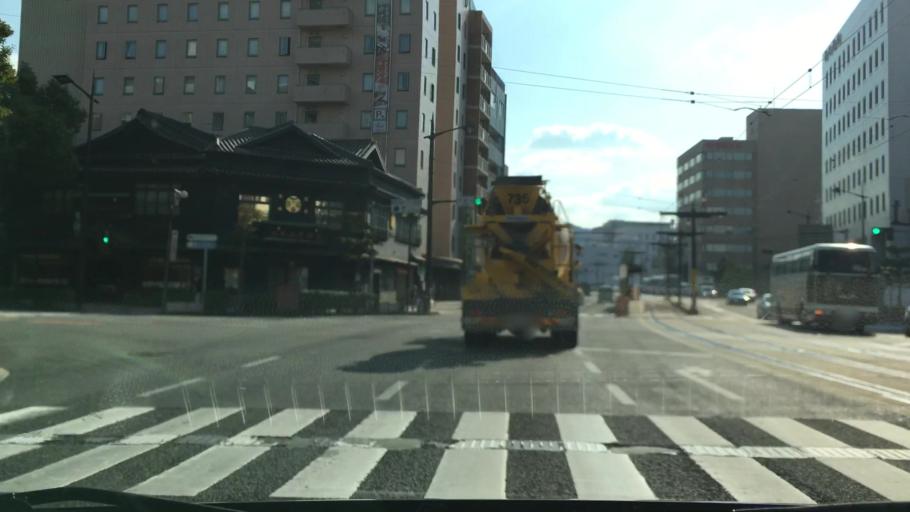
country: JP
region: Nagasaki
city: Nagasaki-shi
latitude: 32.7460
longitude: 129.8722
